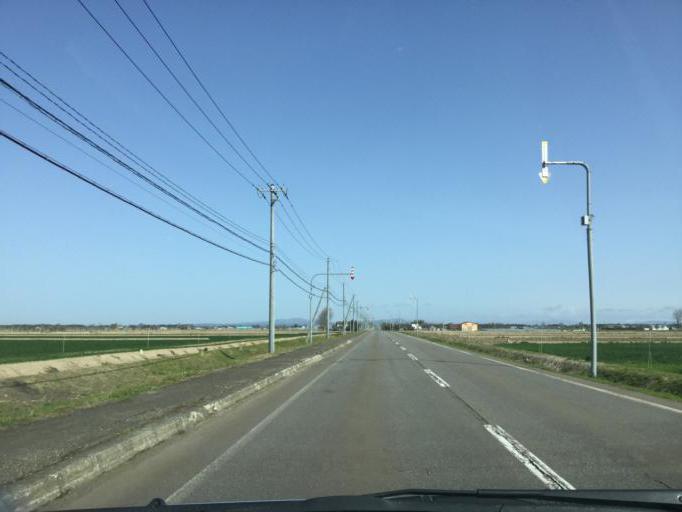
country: JP
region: Hokkaido
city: Iwamizawa
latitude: 43.1546
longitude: 141.7123
